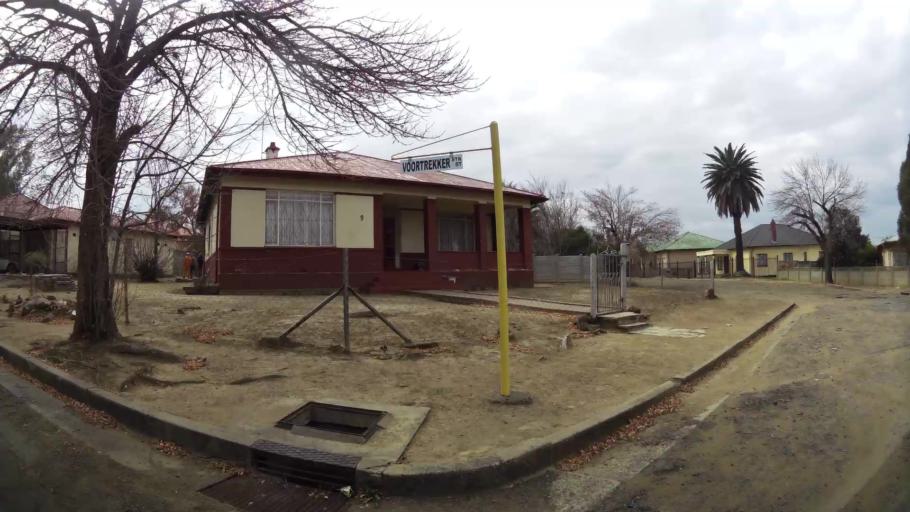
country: ZA
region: Orange Free State
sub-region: Fezile Dabi District Municipality
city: Kroonstad
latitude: -27.6543
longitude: 27.2334
